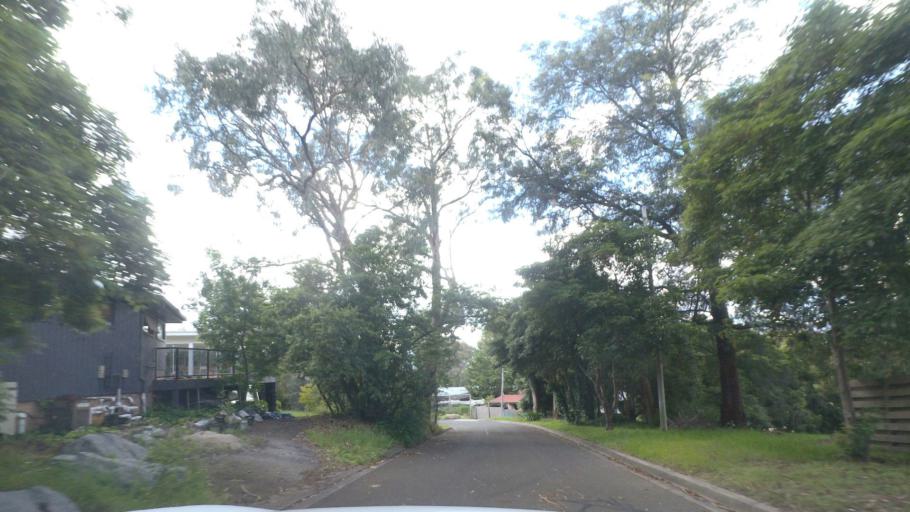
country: AU
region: Victoria
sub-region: Maroondah
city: Croydon South
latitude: -37.8112
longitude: 145.2633
